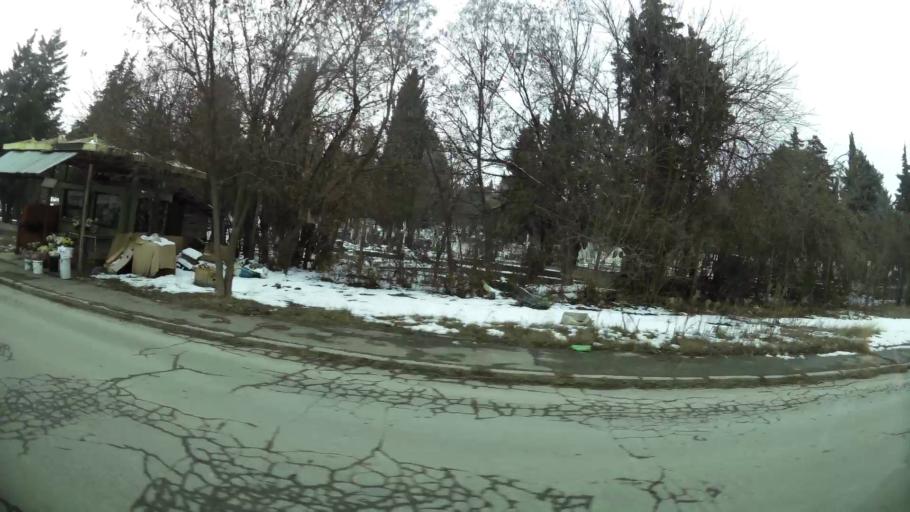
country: MK
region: Butel
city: Butel
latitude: 42.0384
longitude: 21.4373
